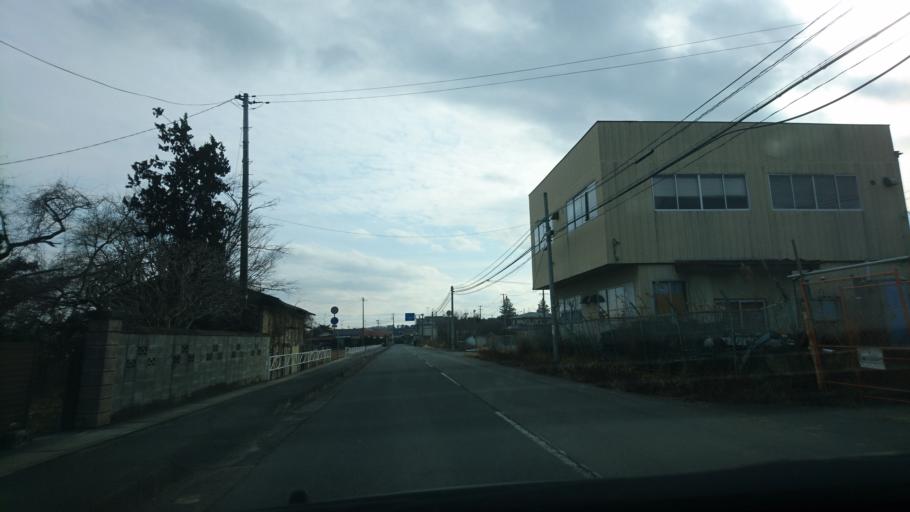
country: JP
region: Iwate
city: Ichinoseki
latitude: 38.8501
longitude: 141.1721
